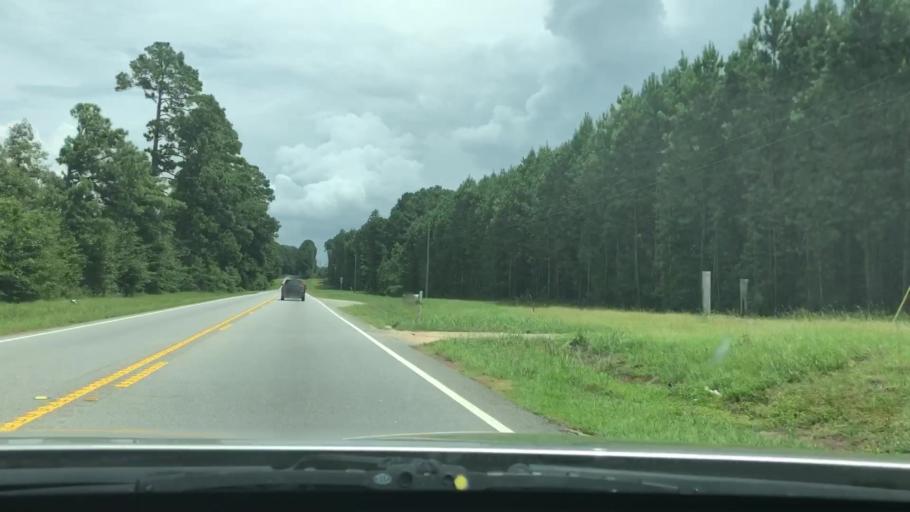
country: US
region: Georgia
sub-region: Lamar County
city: Barnesville
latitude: 33.1538
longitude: -84.1264
